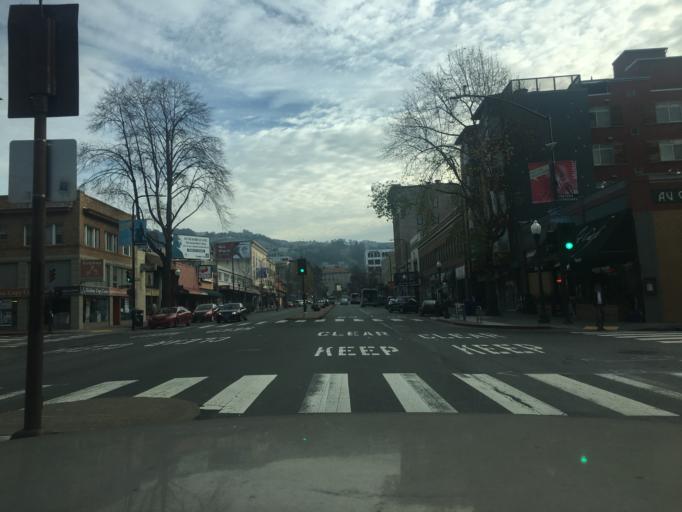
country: US
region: California
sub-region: Alameda County
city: Berkeley
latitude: 37.8718
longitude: -122.2711
